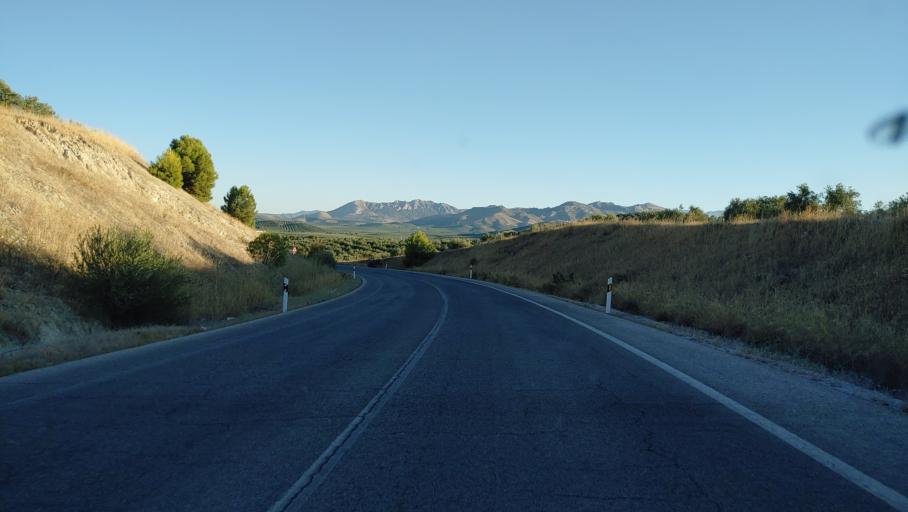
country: ES
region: Andalusia
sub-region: Provincia de Jaen
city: Ubeda
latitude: 37.9312
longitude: -3.3560
